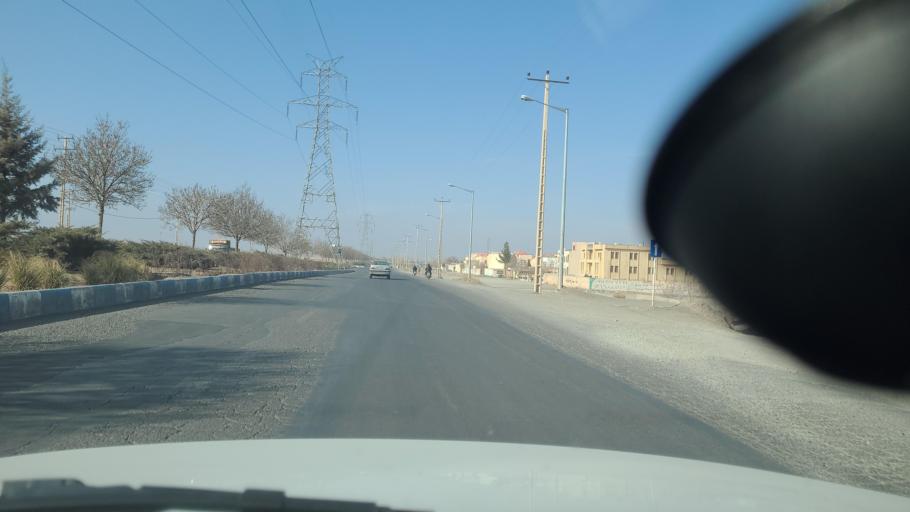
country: IR
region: Razavi Khorasan
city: Fariman
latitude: 35.6961
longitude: 59.8419
